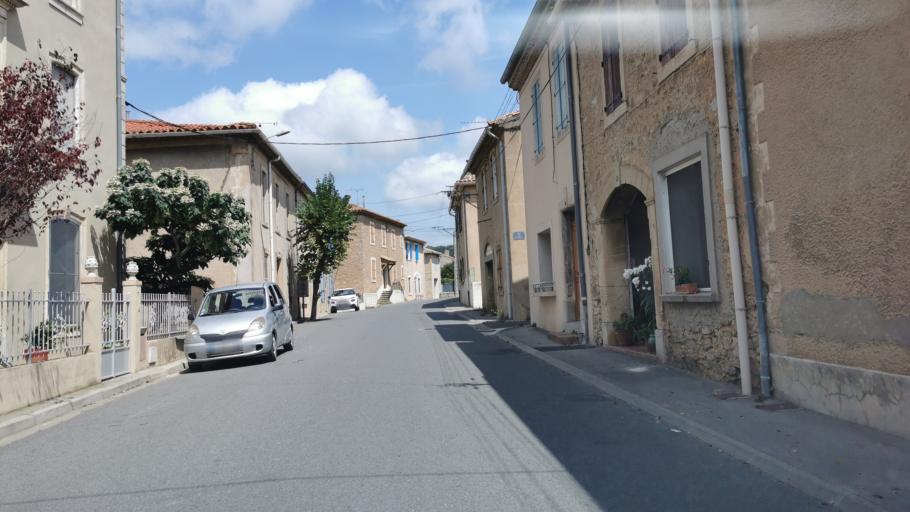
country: FR
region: Languedoc-Roussillon
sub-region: Departement de l'Aude
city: Bizanet
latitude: 43.1662
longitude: 2.8717
